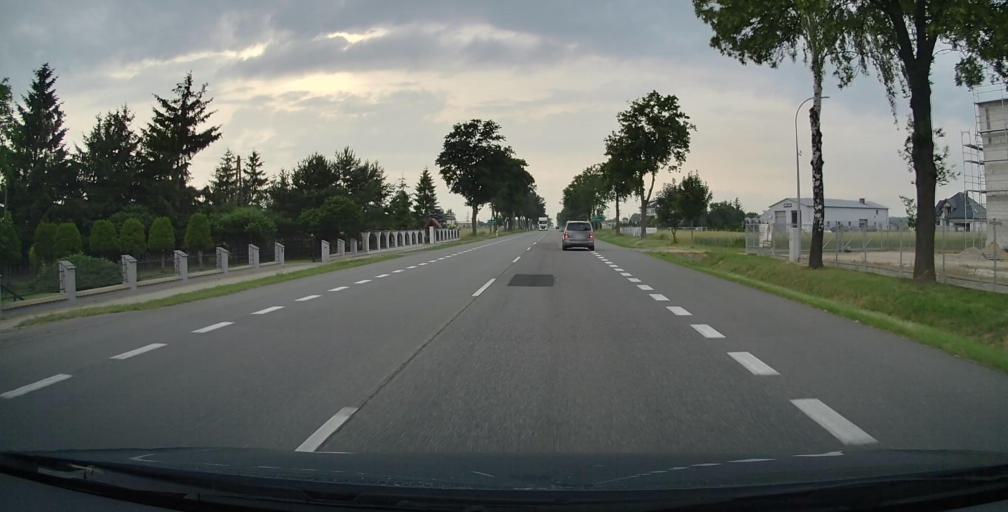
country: PL
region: Masovian Voivodeship
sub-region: Powiat siedlecki
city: Zbuczyn
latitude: 52.1102
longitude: 22.3818
